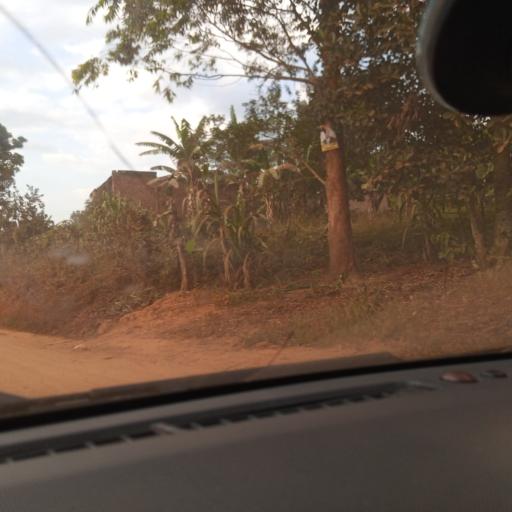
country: UG
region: Central Region
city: Masaka
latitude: -0.3535
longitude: 31.7210
